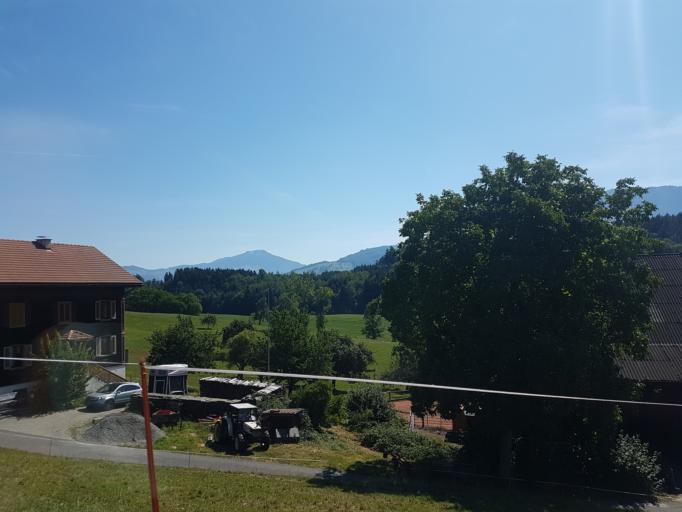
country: CH
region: Lucerne
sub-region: Lucerne-Land District
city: Udligenswil
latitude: 47.0845
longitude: 8.3992
